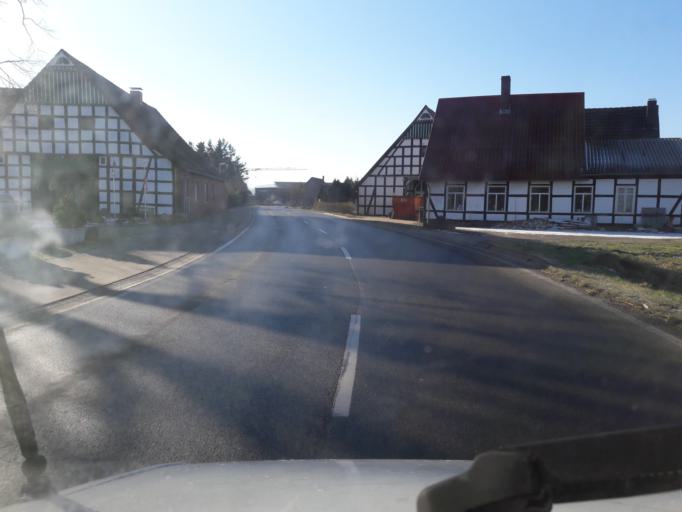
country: DE
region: North Rhine-Westphalia
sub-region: Regierungsbezirk Detmold
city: Hille
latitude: 52.3297
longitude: 8.7456
